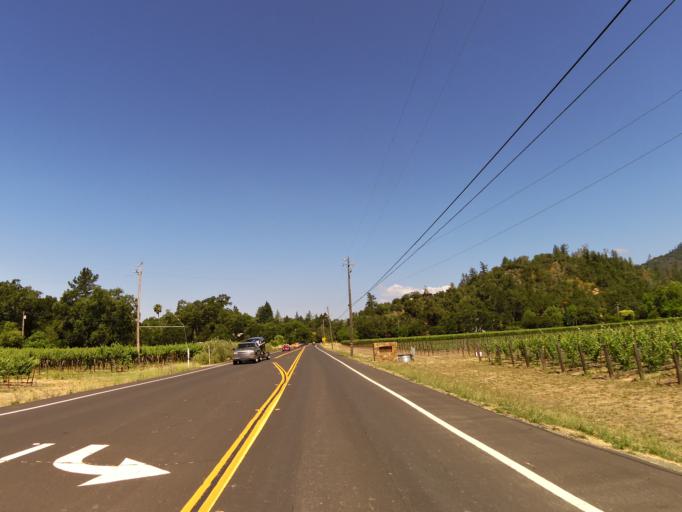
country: US
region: California
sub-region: Napa County
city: Deer Park
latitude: 38.5547
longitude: -122.5012
